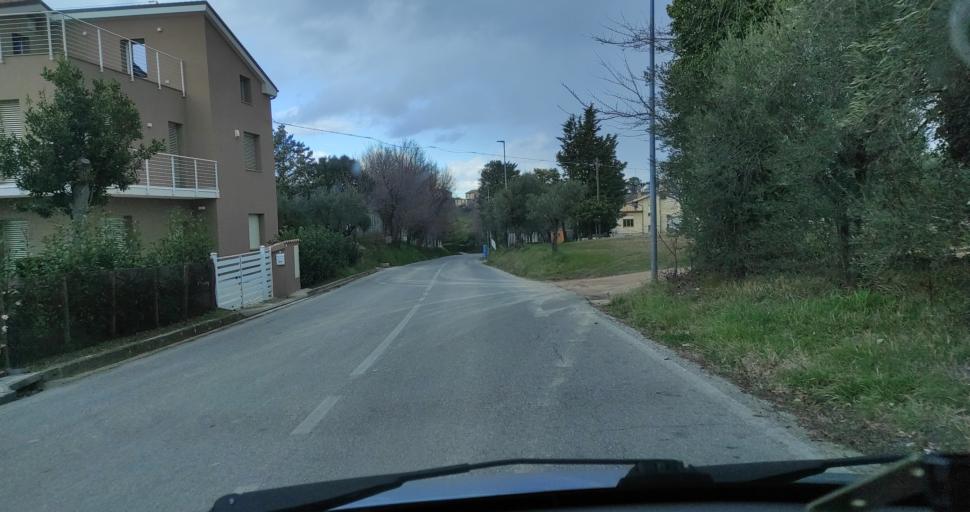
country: IT
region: The Marches
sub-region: Provincia di Macerata
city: Mogliano
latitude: 43.1901
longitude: 13.4700
